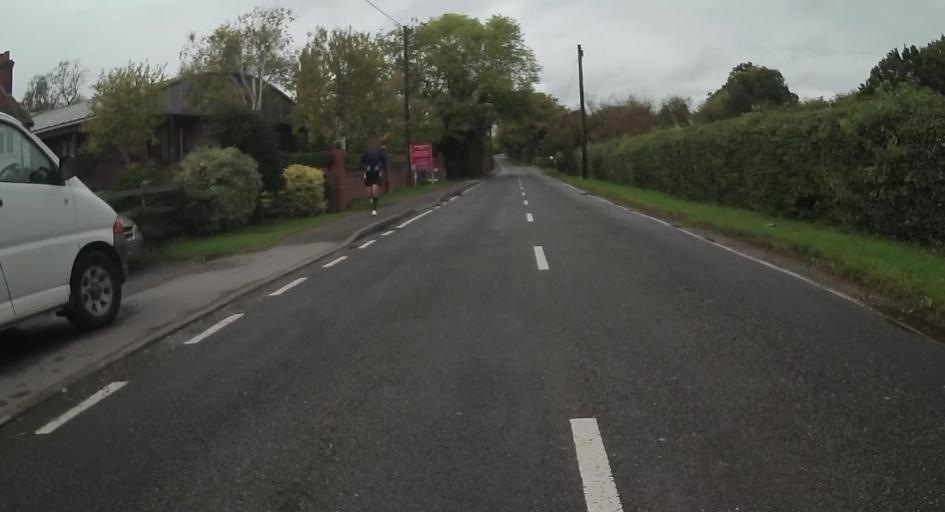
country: GB
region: England
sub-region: Hampshire
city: Tadley
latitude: 51.3488
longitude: -1.1653
